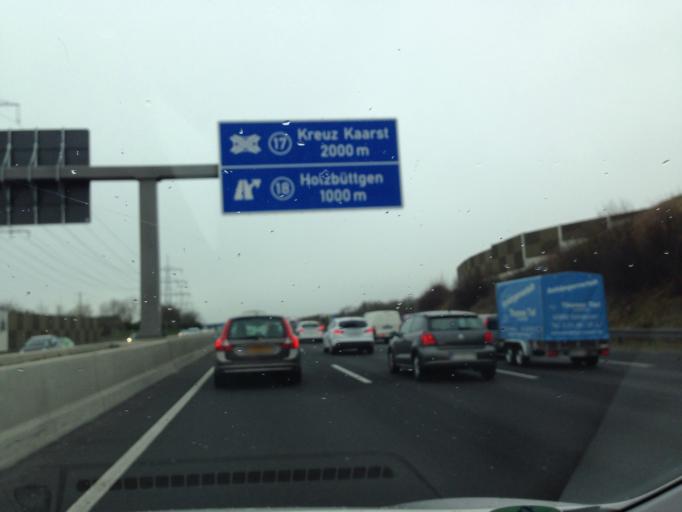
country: DE
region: North Rhine-Westphalia
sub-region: Regierungsbezirk Dusseldorf
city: Neuss
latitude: 51.2061
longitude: 6.6497
